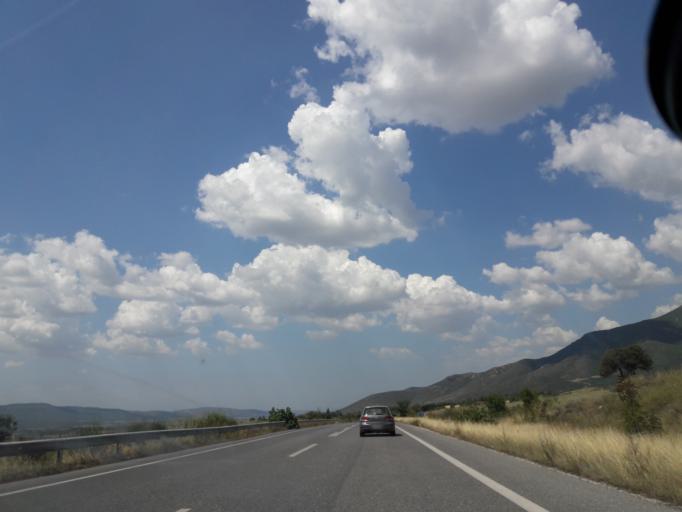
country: GR
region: Central Macedonia
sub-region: Nomos Chalkidikis
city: Galatista
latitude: 40.4656
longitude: 23.2587
